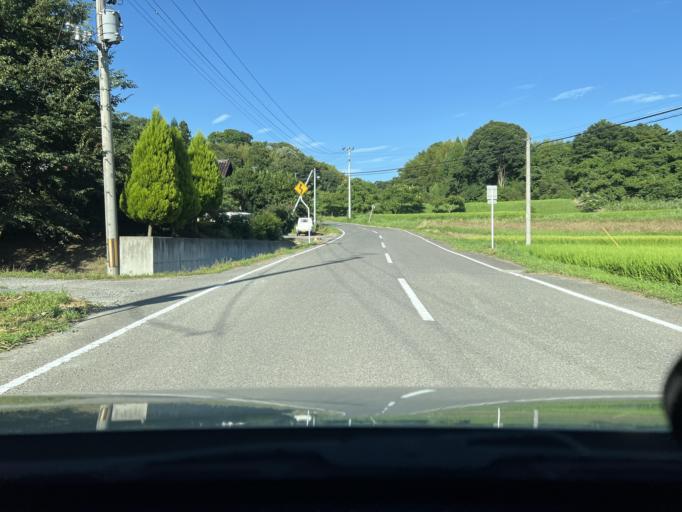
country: JP
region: Fukushima
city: Miharu
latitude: 37.4337
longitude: 140.4413
